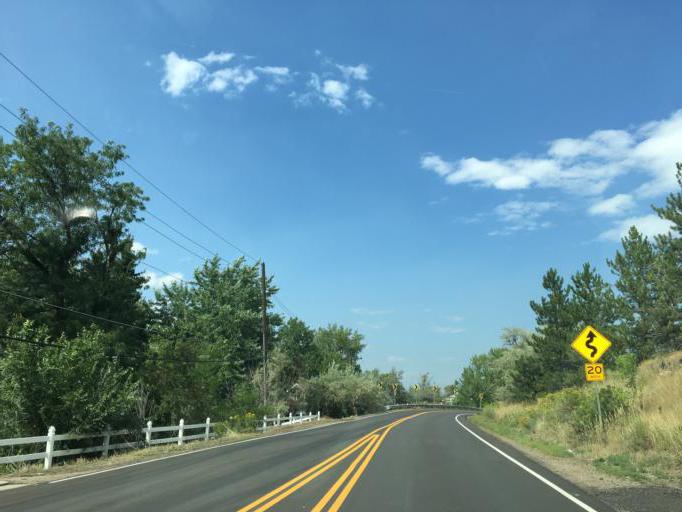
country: US
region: Colorado
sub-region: Jefferson County
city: Applewood
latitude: 39.7482
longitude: -105.1283
